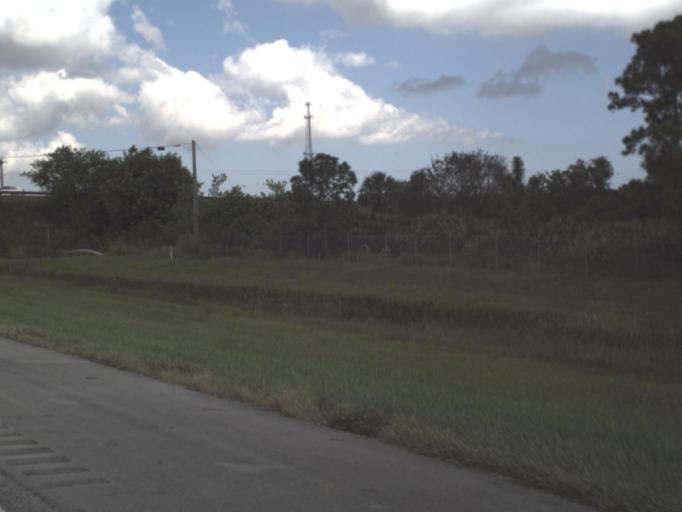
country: US
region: Florida
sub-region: Saint Lucie County
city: Fort Pierce South
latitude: 27.3734
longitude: -80.3834
